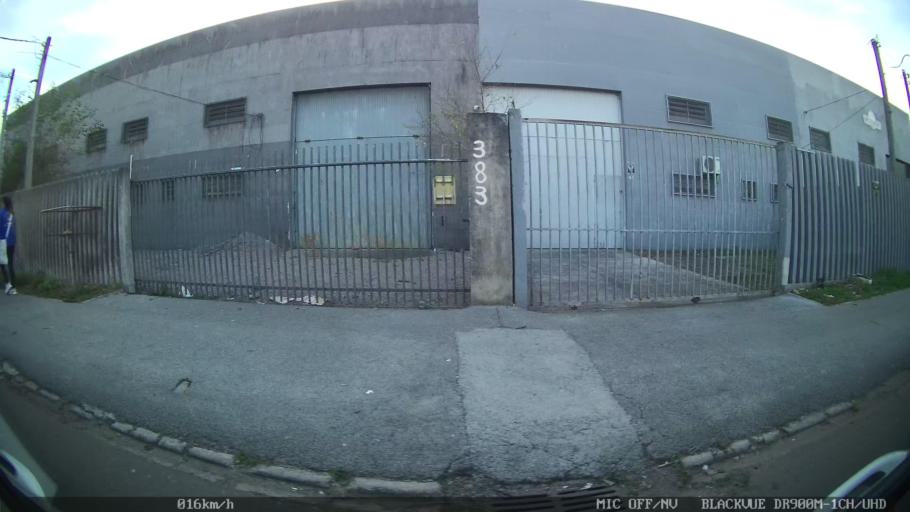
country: BR
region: Parana
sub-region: Pinhais
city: Pinhais
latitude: -25.4467
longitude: -49.1761
